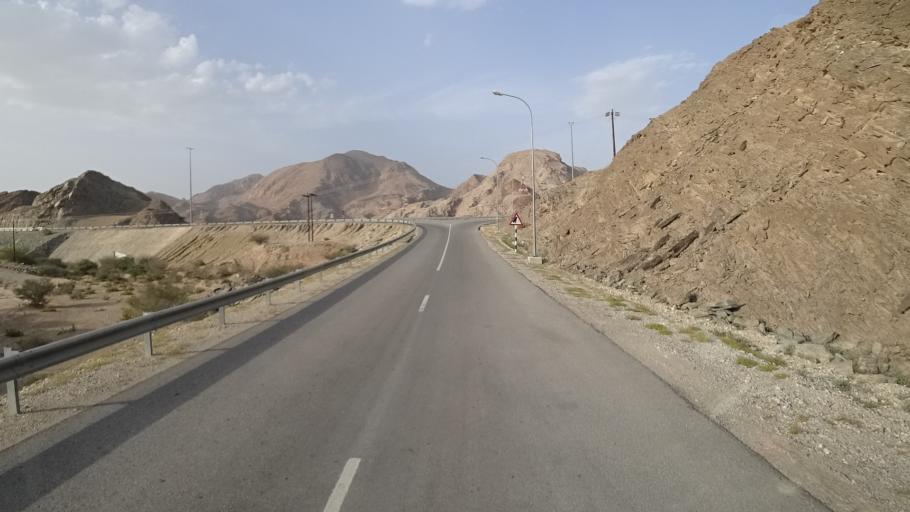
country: OM
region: Muhafazat Masqat
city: Bawshar
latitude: 23.3519
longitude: 58.5333
